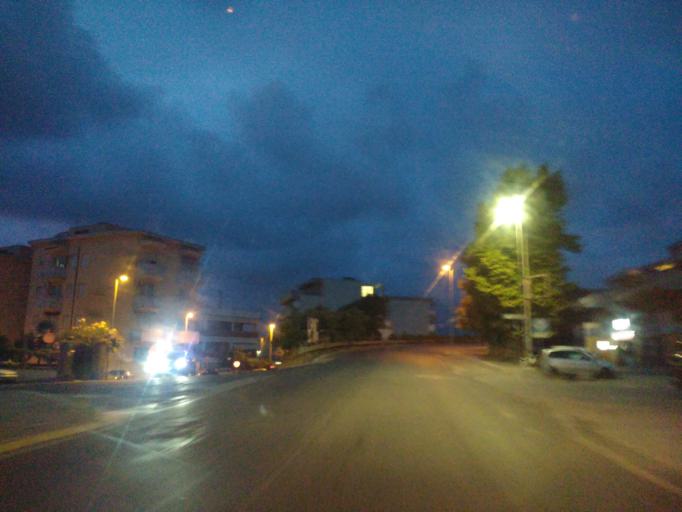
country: IT
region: Latium
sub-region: Citta metropolitana di Roma Capitale
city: Anzio
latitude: 41.4521
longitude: 12.6234
